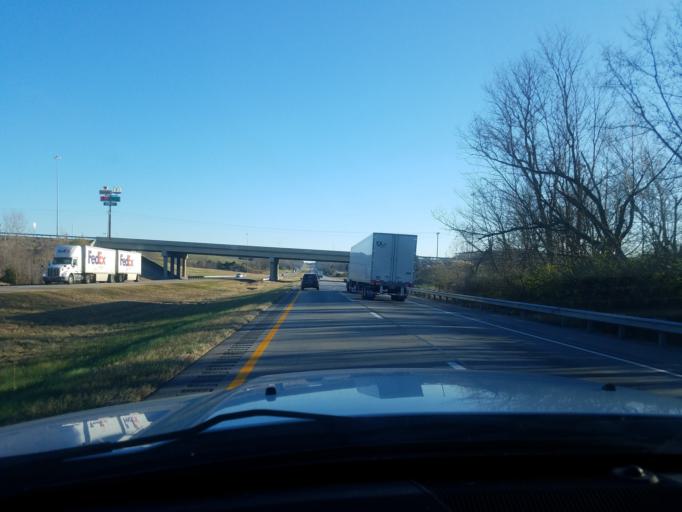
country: US
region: Kentucky
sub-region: Gallatin County
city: Warsaw
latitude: 38.6909
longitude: -84.9399
